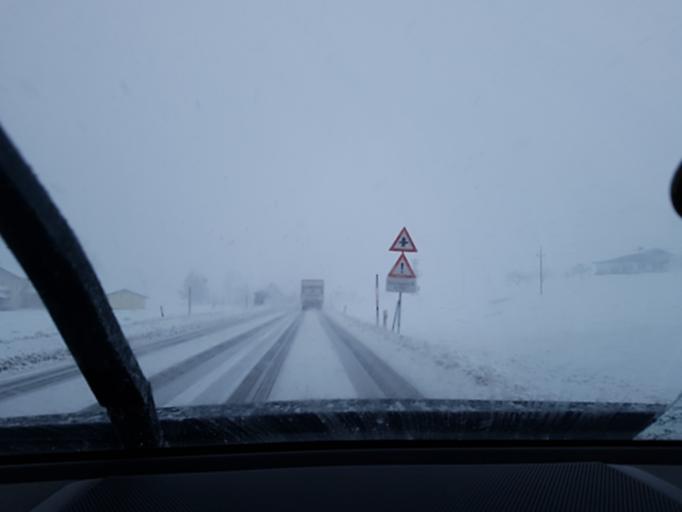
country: AT
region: Salzburg
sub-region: Politischer Bezirk Hallein
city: Abtenau
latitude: 47.5739
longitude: 13.3300
